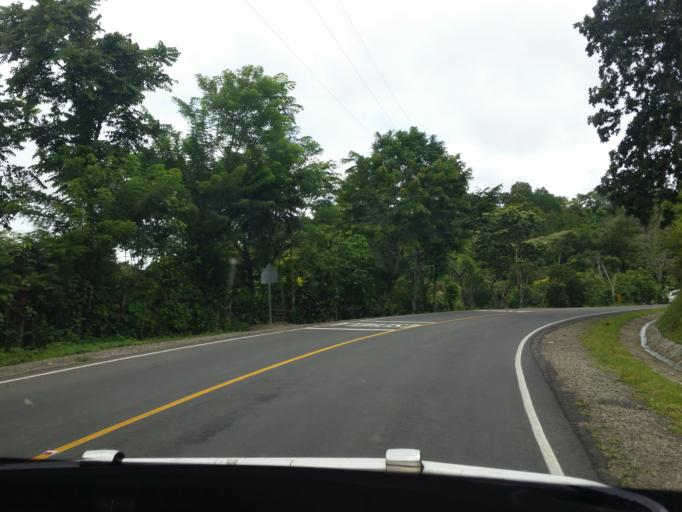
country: NI
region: Jinotega
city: Jinotega
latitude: 13.1480
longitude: -85.9583
